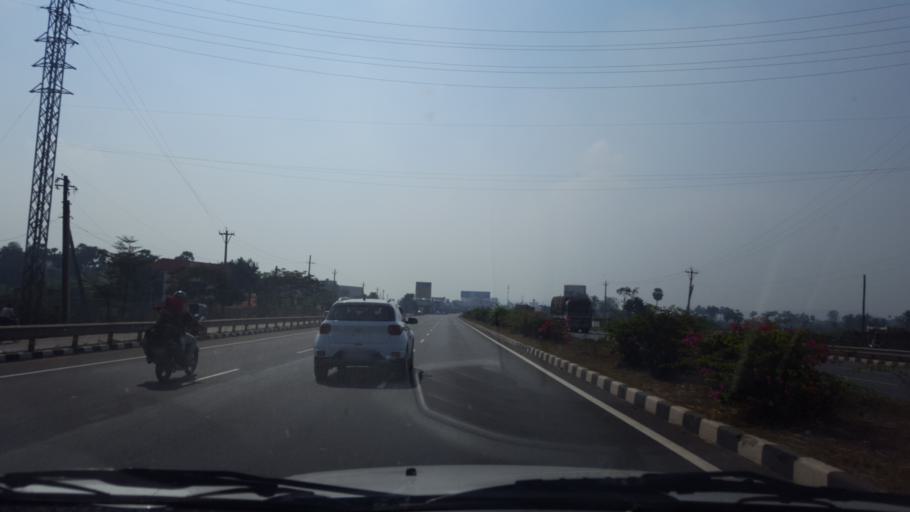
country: IN
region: Andhra Pradesh
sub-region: Vishakhapatnam
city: Bhimunipatnam
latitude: 17.9457
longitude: 83.4190
